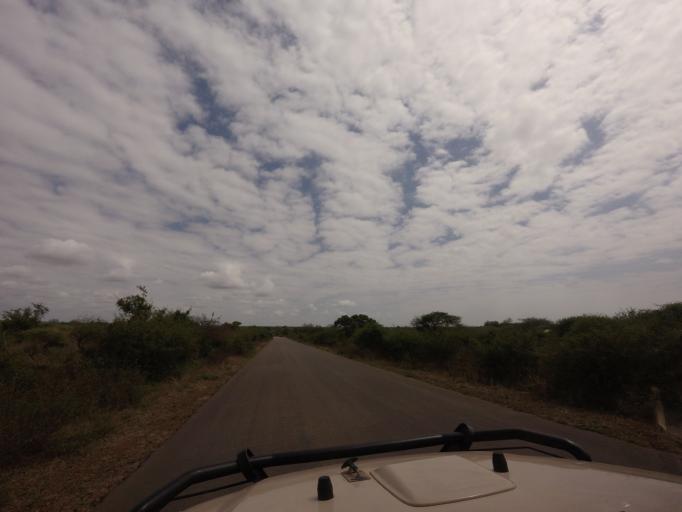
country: ZA
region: Mpumalanga
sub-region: Ehlanzeni District
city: Komatipoort
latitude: -25.1195
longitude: 31.9138
